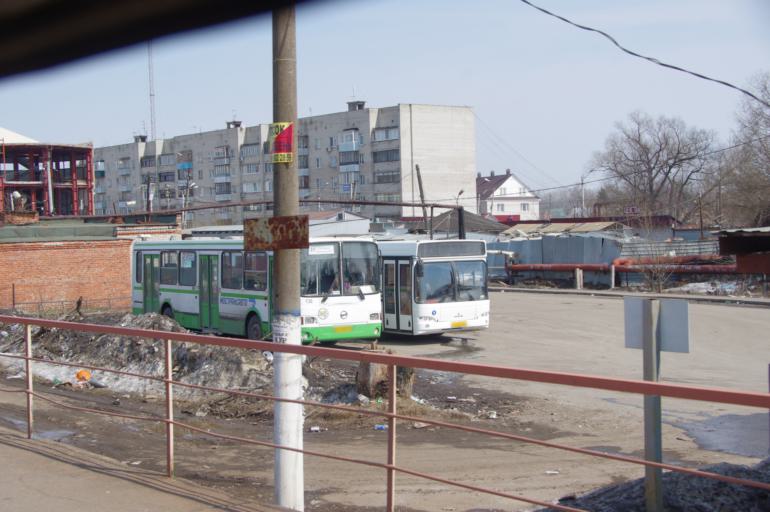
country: RU
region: Moskovskaya
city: Stolbovaya
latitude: 55.2479
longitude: 37.4936
